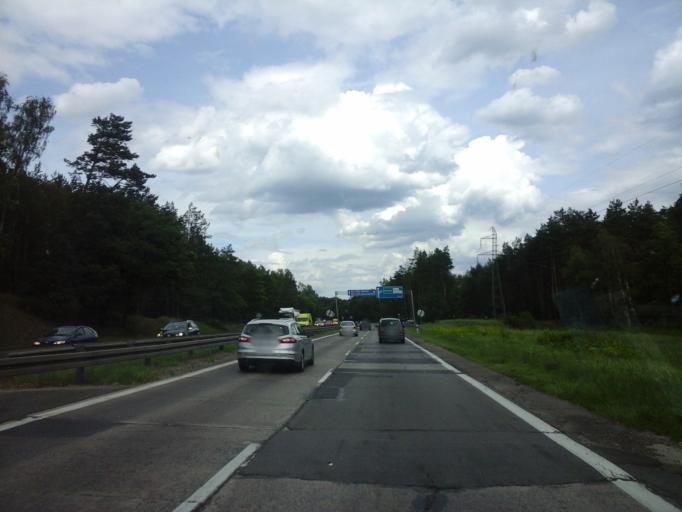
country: PL
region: West Pomeranian Voivodeship
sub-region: Powiat gryfinski
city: Stare Czarnowo
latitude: 53.3794
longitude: 14.7080
